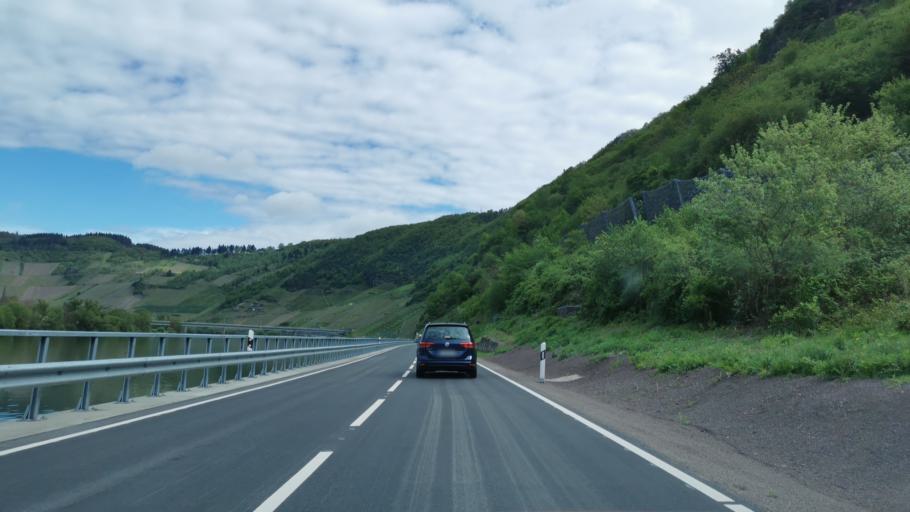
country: DE
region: Rheinland-Pfalz
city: Enkirch
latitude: 49.9702
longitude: 7.1062
